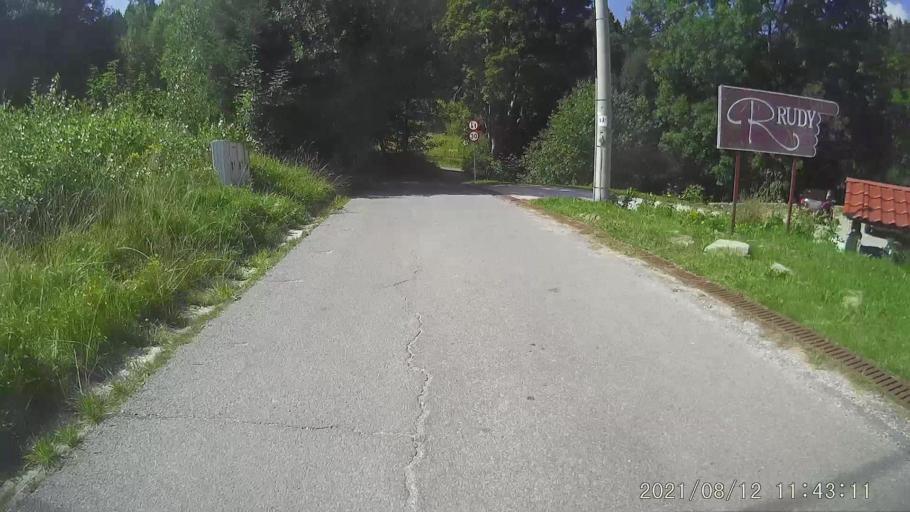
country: PL
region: Lower Silesian Voivodeship
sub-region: Powiat klodzki
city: Stronie Slaskie
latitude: 50.2638
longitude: 16.8329
